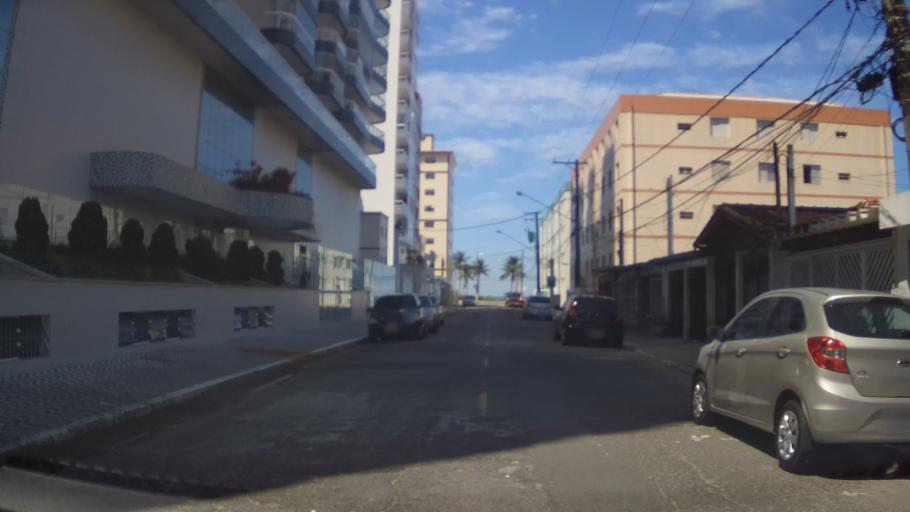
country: BR
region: Sao Paulo
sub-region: Praia Grande
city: Praia Grande
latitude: -24.0255
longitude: -46.4667
